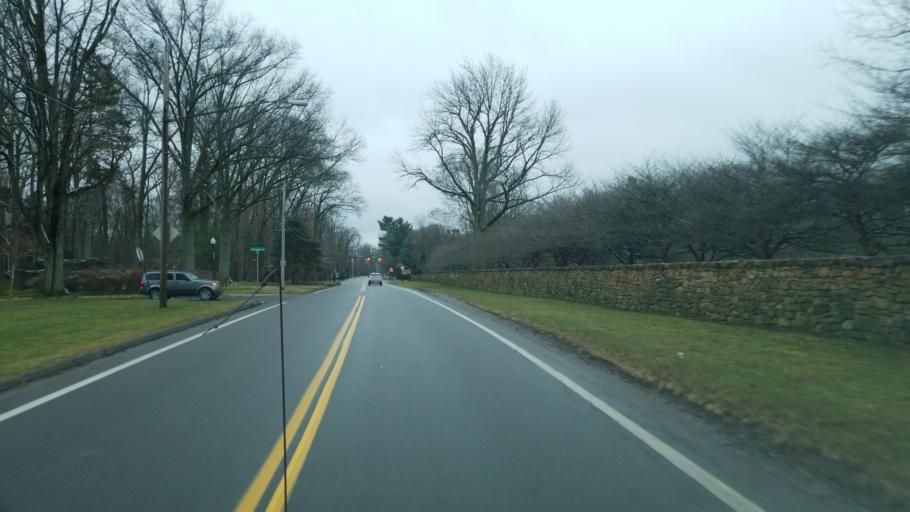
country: US
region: Ohio
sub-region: Summit County
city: Akron
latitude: 41.1181
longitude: -81.5486
